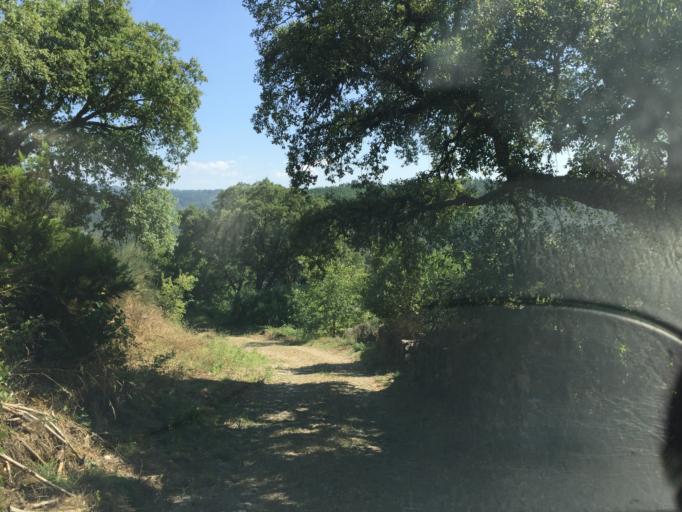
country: PT
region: Leiria
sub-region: Pedrogao Grande
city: Pedrogao Grande
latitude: 39.9049
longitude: -8.1441
